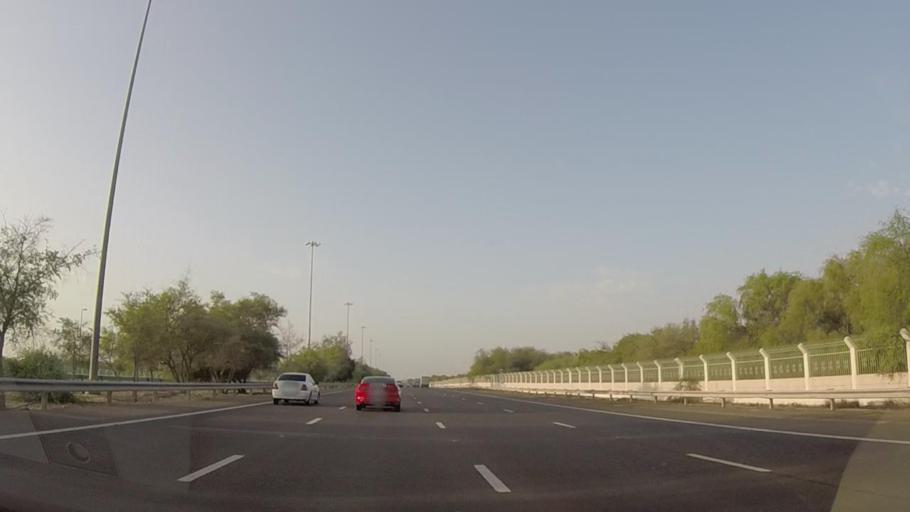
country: AE
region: Dubai
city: Dubai
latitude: 24.8271
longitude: 54.8802
